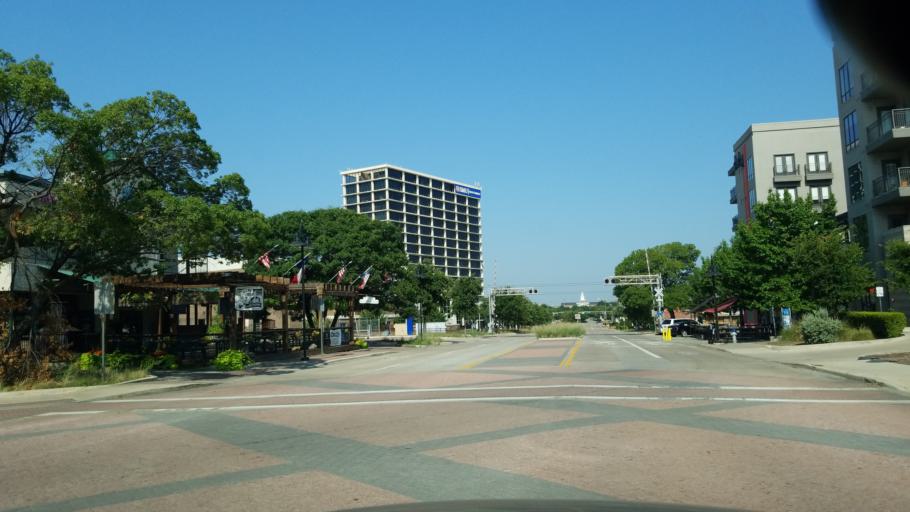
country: US
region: Texas
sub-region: Dallas County
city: Highland Park
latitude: 32.8420
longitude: -96.7716
